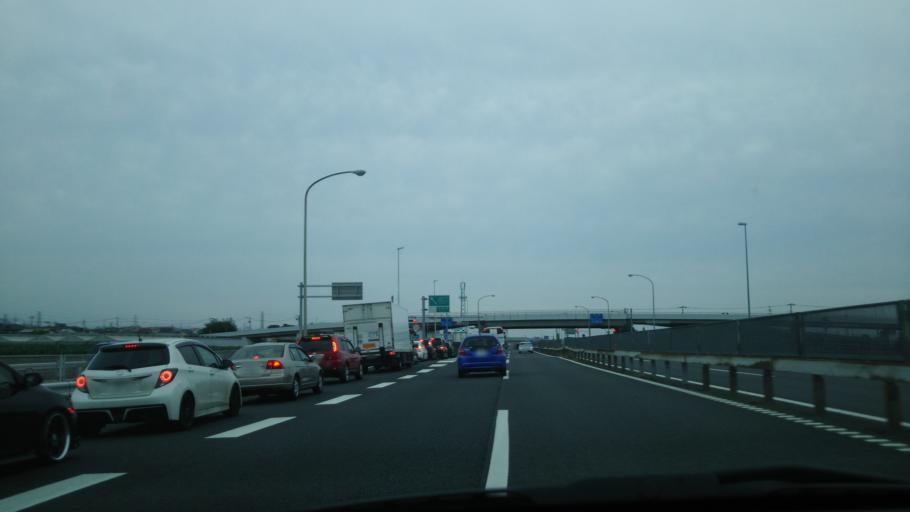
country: JP
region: Kanagawa
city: Isehara
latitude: 35.3844
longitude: 139.3307
